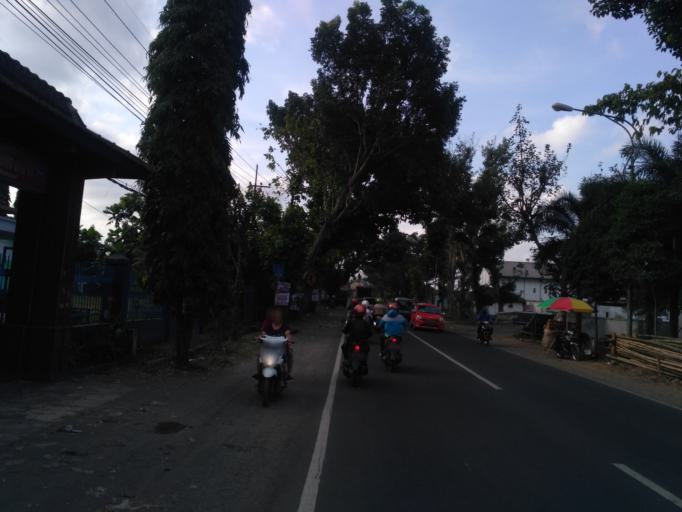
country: ID
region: East Java
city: Wadung
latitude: -8.0440
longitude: 112.6081
